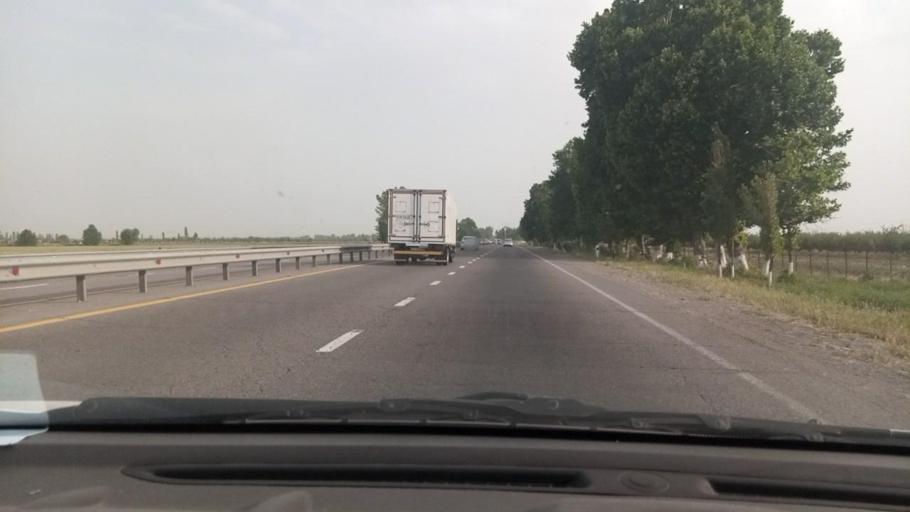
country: UZ
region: Toshkent Shahri
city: Bektemir
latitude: 41.1963
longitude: 69.4030
